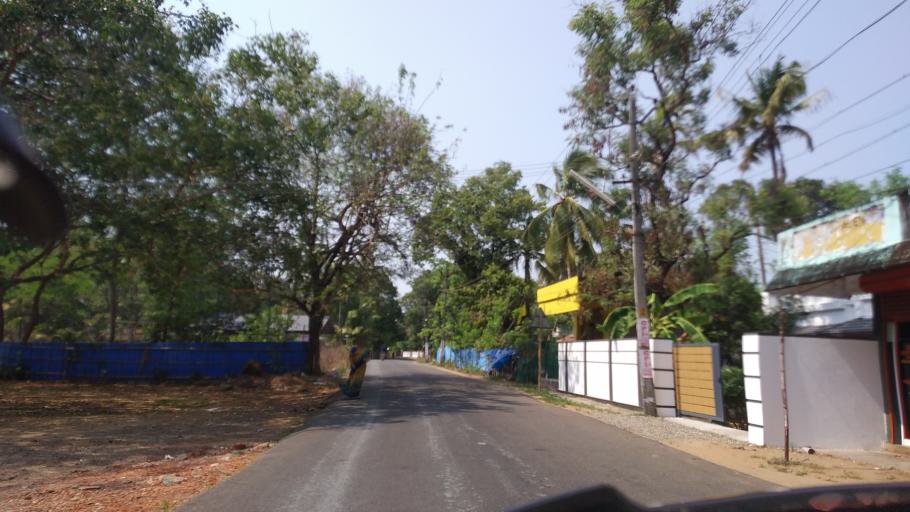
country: IN
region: Kerala
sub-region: Thrissur District
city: Thanniyam
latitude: 10.3414
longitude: 76.1170
